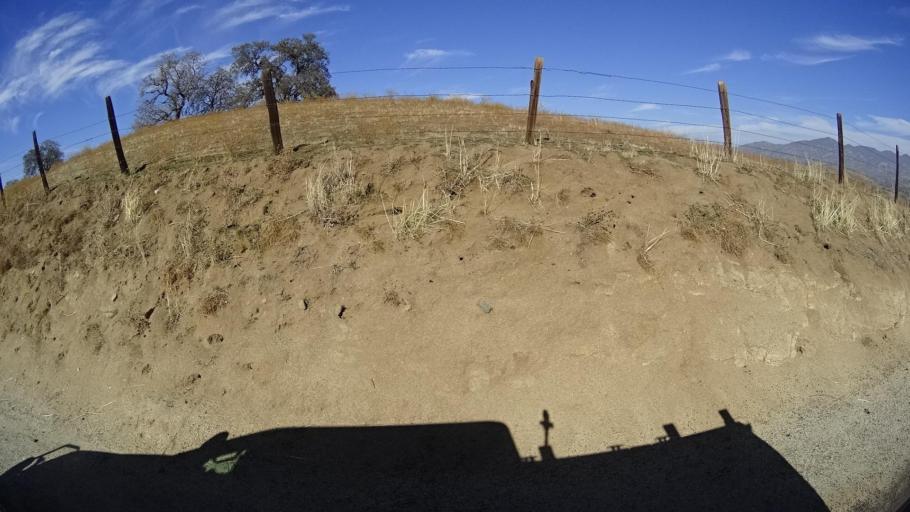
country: US
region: California
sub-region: Tulare County
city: Richgrove
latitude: 35.6929
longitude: -118.8682
